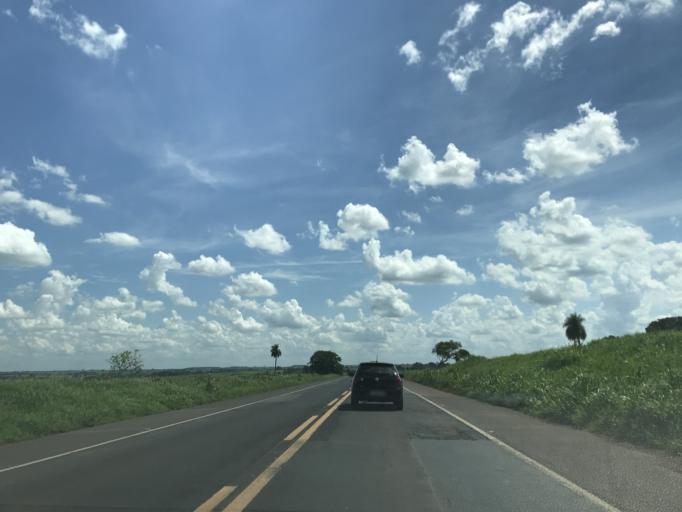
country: BR
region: Sao Paulo
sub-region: Nova Granada
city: Nova Granada
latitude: -20.4606
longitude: -49.2887
